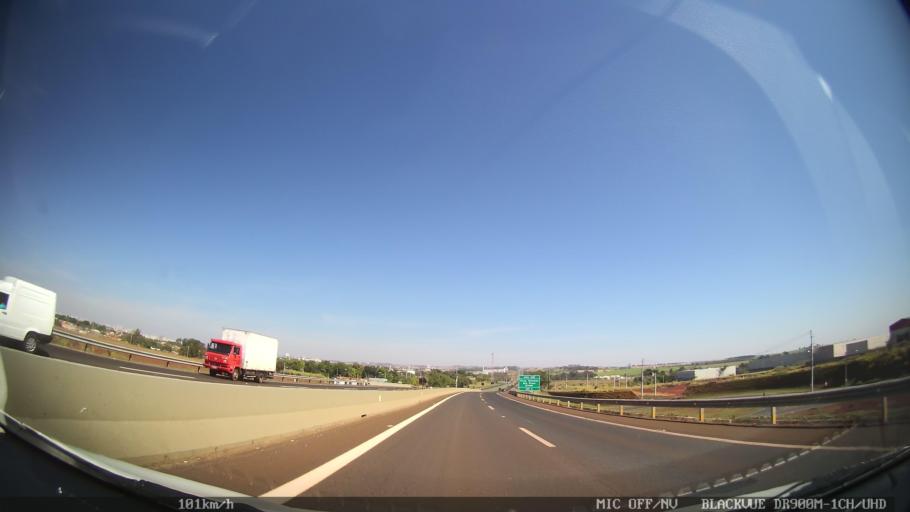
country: BR
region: Sao Paulo
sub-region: Ribeirao Preto
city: Ribeirao Preto
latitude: -21.1007
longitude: -47.8001
